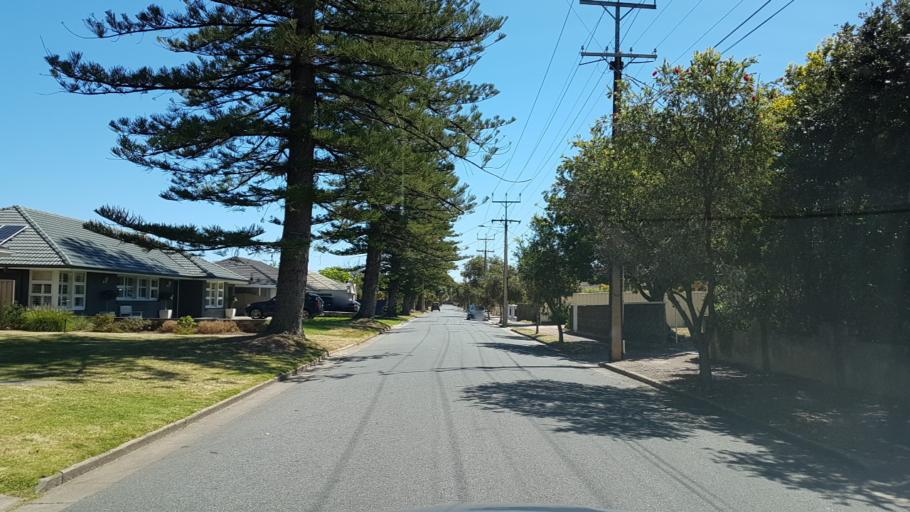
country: AU
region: South Australia
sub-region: Holdfast Bay
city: Glenelg East
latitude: -34.9746
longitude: 138.5266
